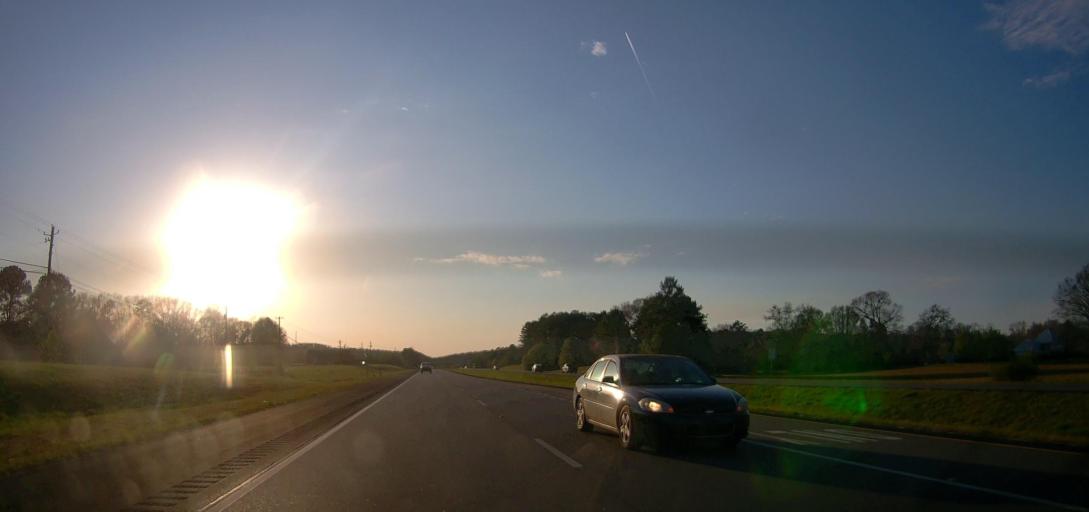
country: US
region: Alabama
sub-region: Shelby County
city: Harpersville
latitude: 33.3481
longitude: -86.4568
